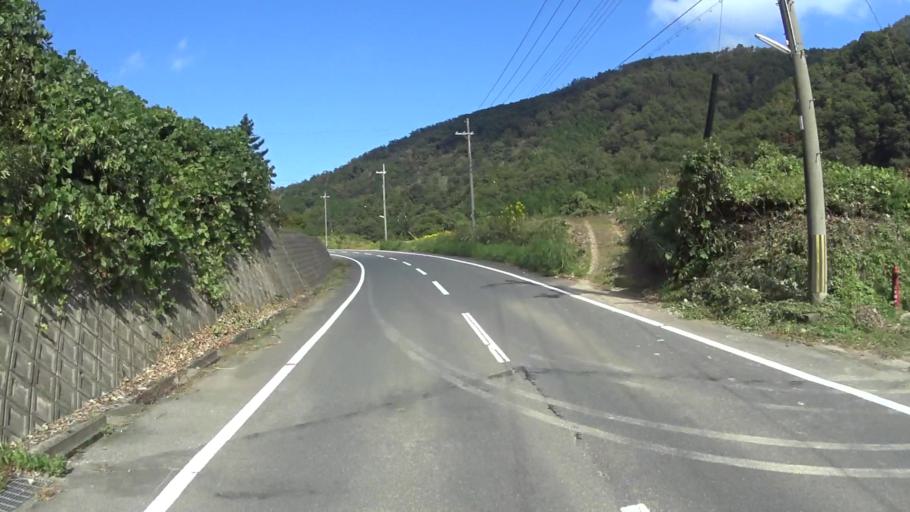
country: JP
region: Kyoto
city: Miyazu
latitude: 35.7056
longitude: 135.2533
